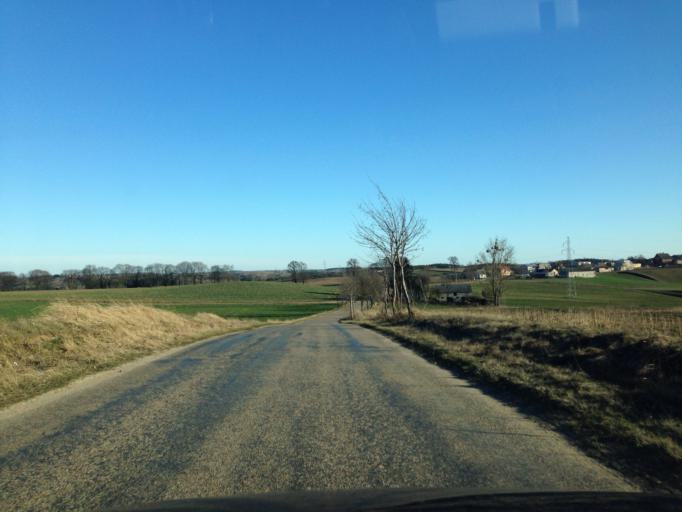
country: PL
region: Kujawsko-Pomorskie
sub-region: Powiat brodnicki
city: Brzozie
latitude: 53.2898
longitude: 19.6536
